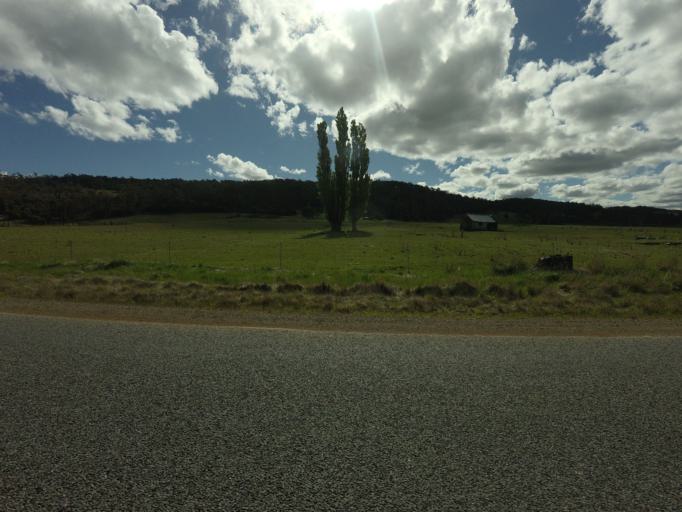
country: AU
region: Tasmania
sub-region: Brighton
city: Bridgewater
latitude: -42.4452
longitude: 147.3126
